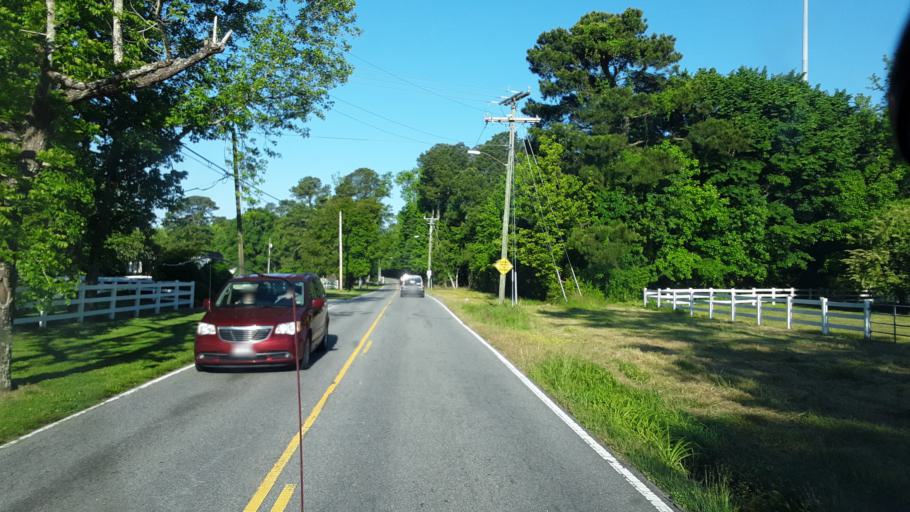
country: US
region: Virginia
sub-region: City of Virginia Beach
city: Virginia Beach
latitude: 36.7235
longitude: -76.0198
